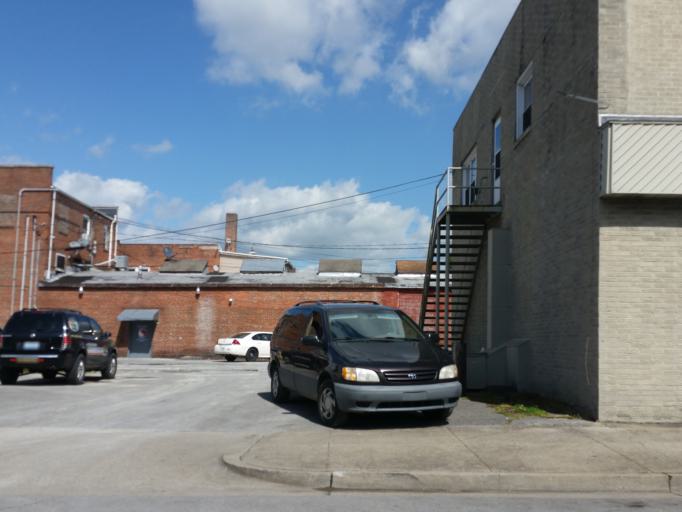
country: US
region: Kentucky
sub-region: Bell County
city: Middlesboro
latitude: 36.6066
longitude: -83.7173
